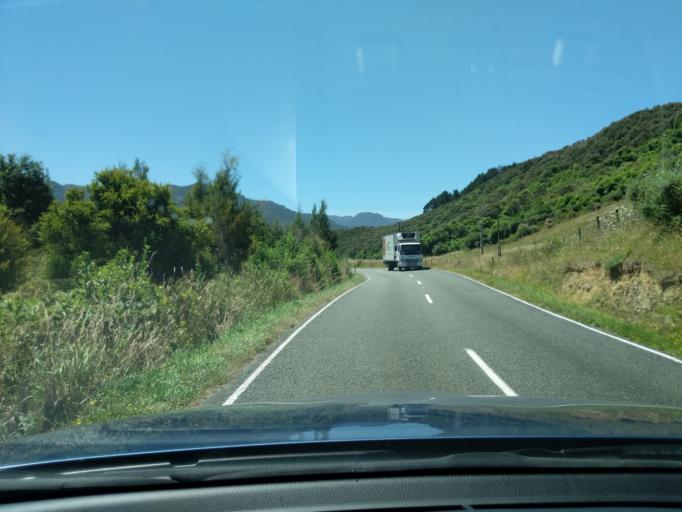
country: NZ
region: Tasman
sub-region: Tasman District
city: Takaka
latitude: -40.7343
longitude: 172.5820
